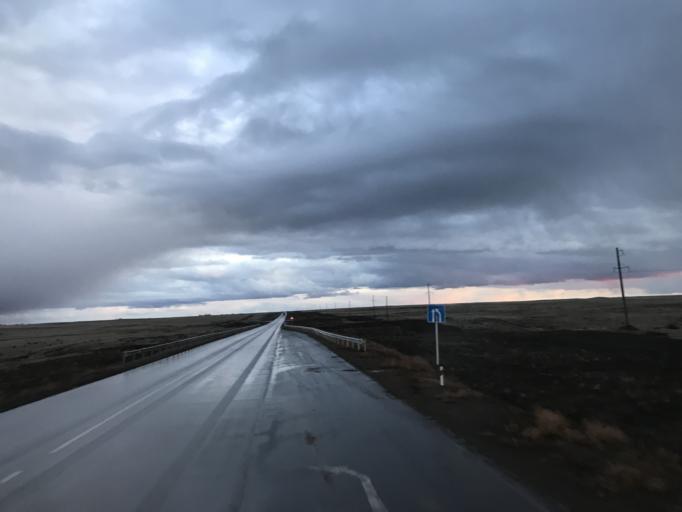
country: KZ
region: Qostanay
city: Ordzhonikidze
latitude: 52.4469
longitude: 61.7728
